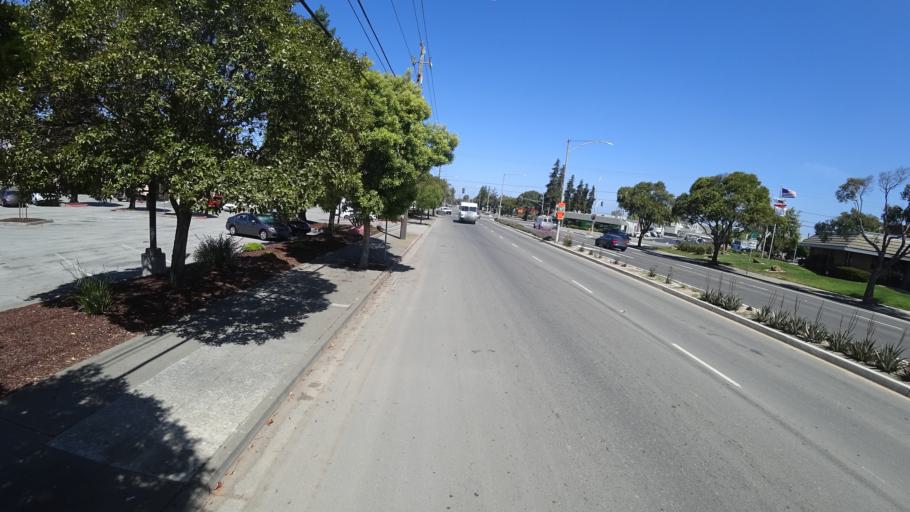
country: US
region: California
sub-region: Alameda County
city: Cherryland
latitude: 37.6379
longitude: -122.1166
